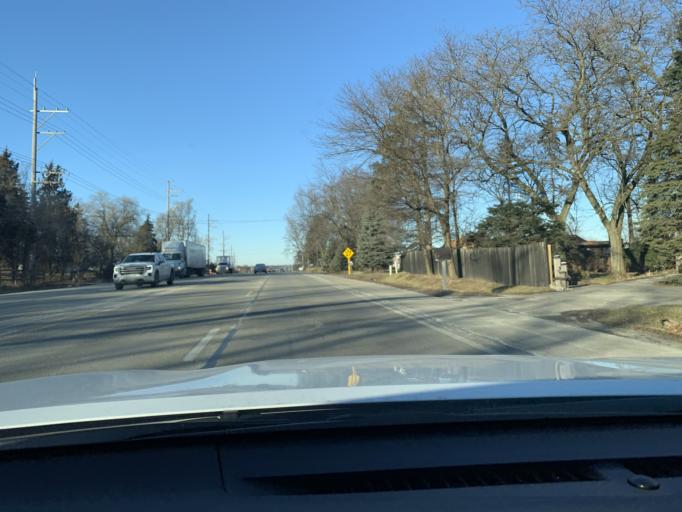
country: US
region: Illinois
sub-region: Cook County
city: Lemont
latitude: 41.7080
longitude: -88.0065
